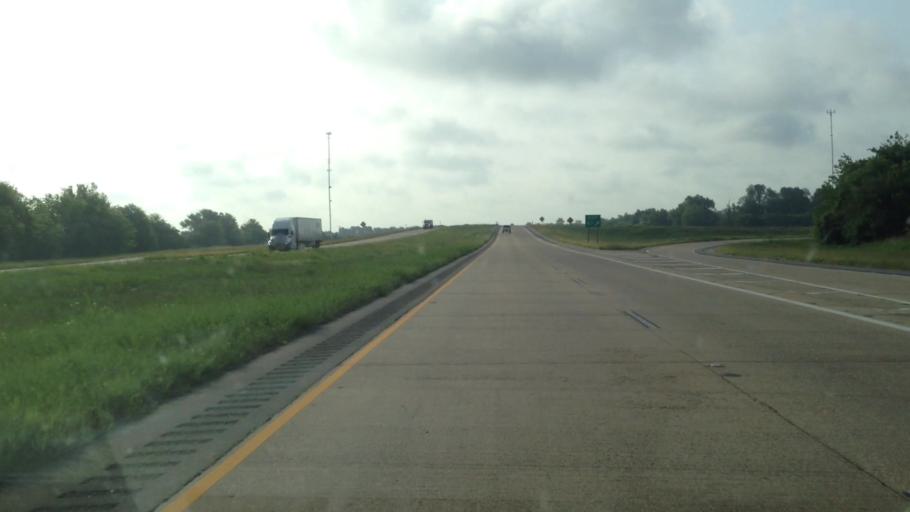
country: US
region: Louisiana
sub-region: Rapides Parish
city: Lecompte
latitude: 31.0163
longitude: -92.3808
